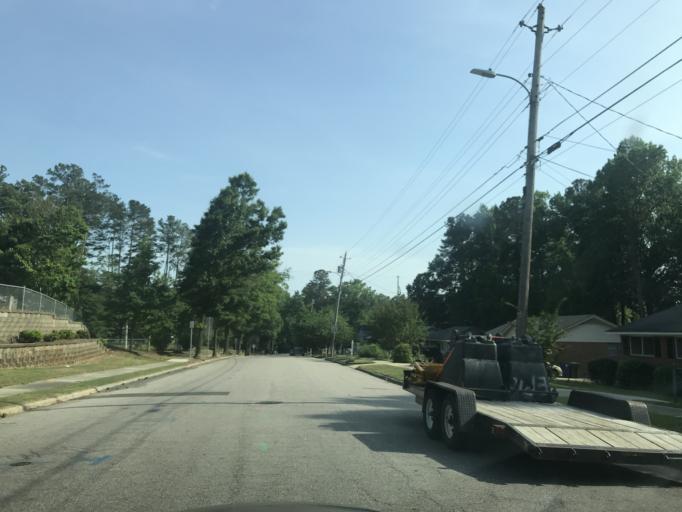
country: US
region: North Carolina
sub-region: Wake County
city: Raleigh
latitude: 35.7652
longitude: -78.5875
